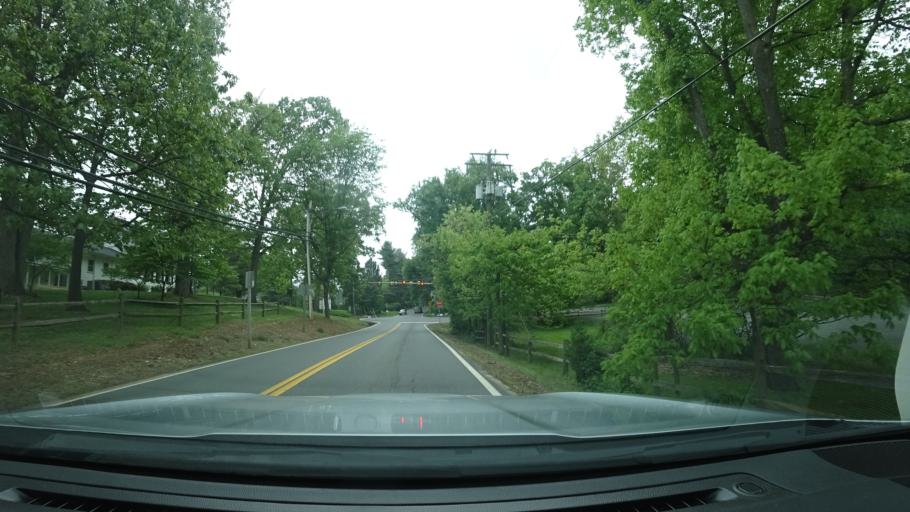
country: US
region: Virginia
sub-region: Fairfax County
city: Oakton
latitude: 38.8915
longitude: -77.3487
